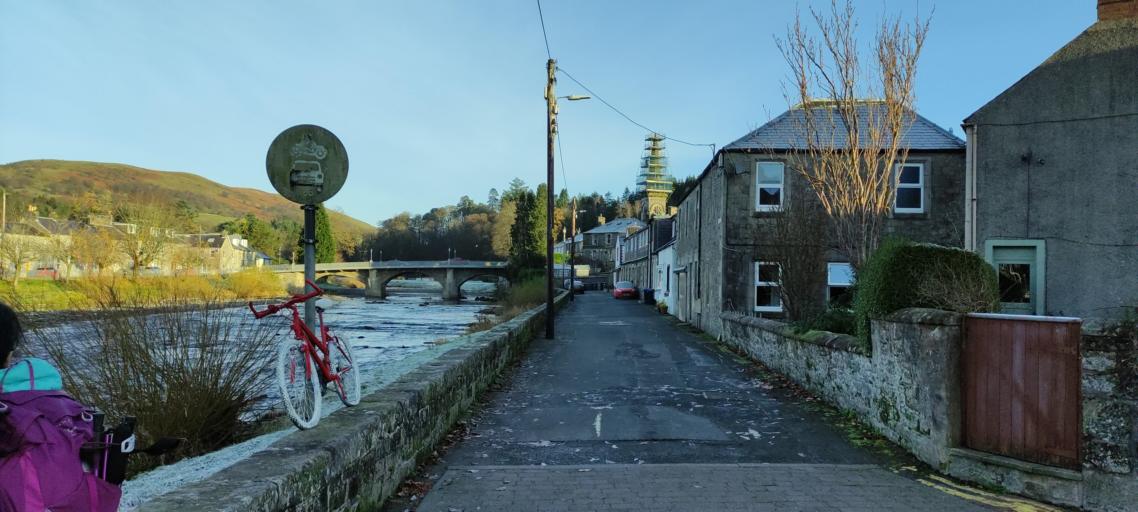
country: GB
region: Scotland
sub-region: Dumfries and Galloway
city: Langholm
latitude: 55.1509
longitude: -3.0016
